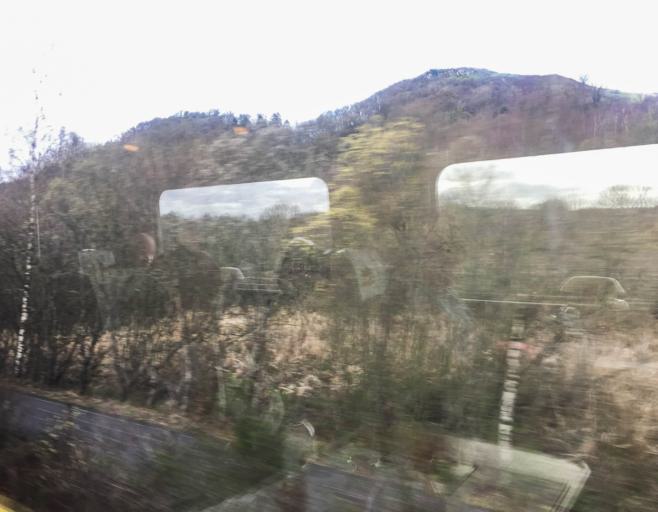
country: GB
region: Scotland
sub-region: Renfrewshire
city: Bishopton
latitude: 55.9331
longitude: -4.5097
